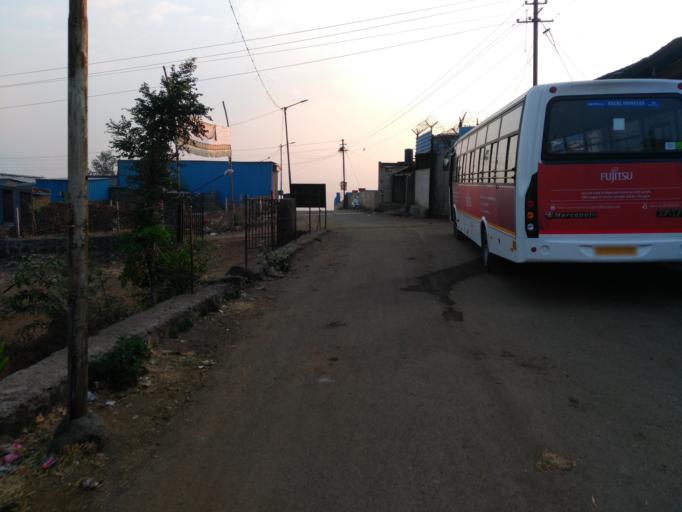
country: IN
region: Maharashtra
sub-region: Pune Division
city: Pune
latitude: 18.4426
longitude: 73.8767
